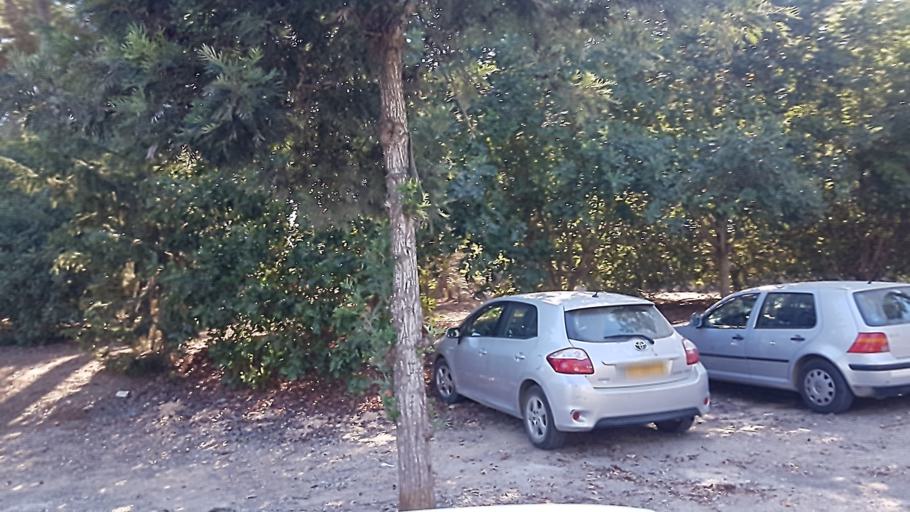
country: IL
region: Central District
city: Kfar Saba
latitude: 32.2113
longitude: 34.9004
